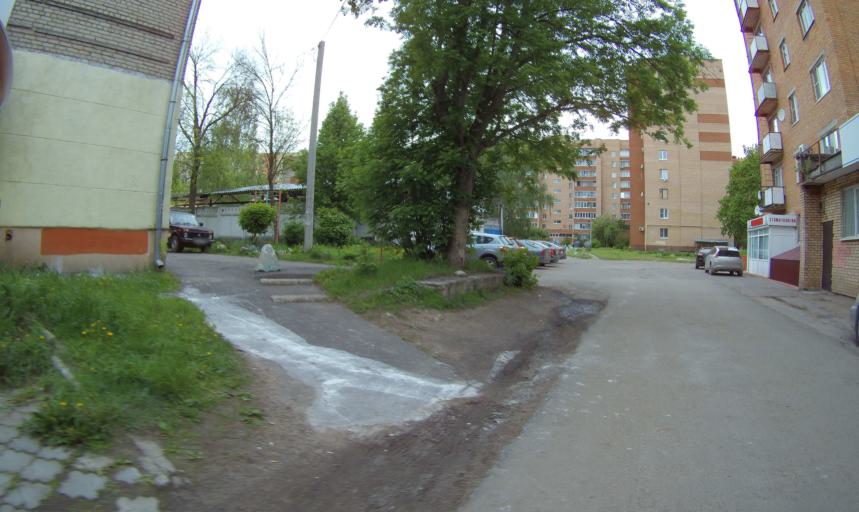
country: RU
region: Moskovskaya
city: Kolomna
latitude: 55.0803
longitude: 38.8075
